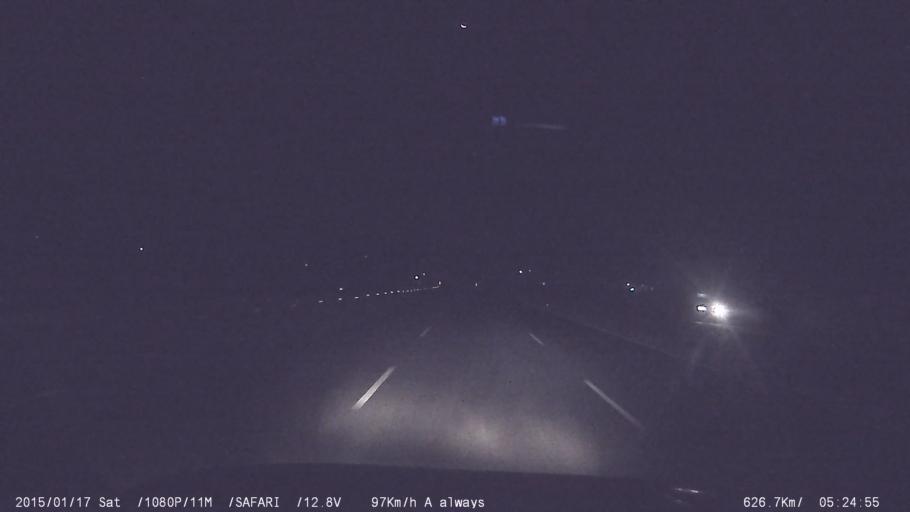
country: IN
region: Tamil Nadu
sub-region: Vellore
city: Katpadi
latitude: 12.9455
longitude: 79.2266
